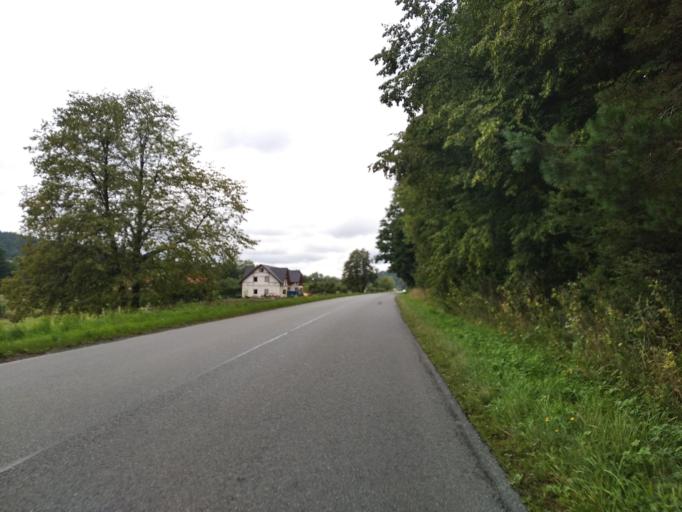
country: PL
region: Subcarpathian Voivodeship
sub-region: Powiat przemyski
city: Bircza
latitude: 49.6859
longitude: 22.4000
